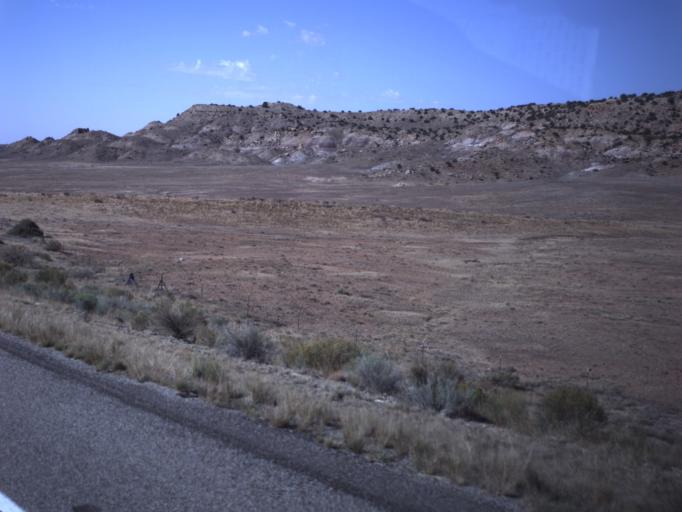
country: US
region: Utah
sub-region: San Juan County
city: Blanding
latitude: 37.4264
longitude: -109.4721
